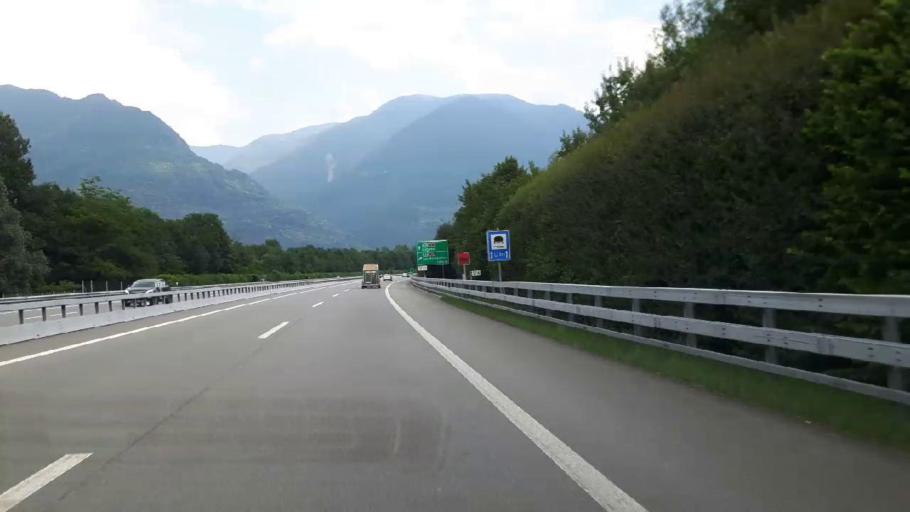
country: CH
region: Ticino
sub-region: Riviera District
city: Claro
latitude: 46.2354
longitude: 9.0293
